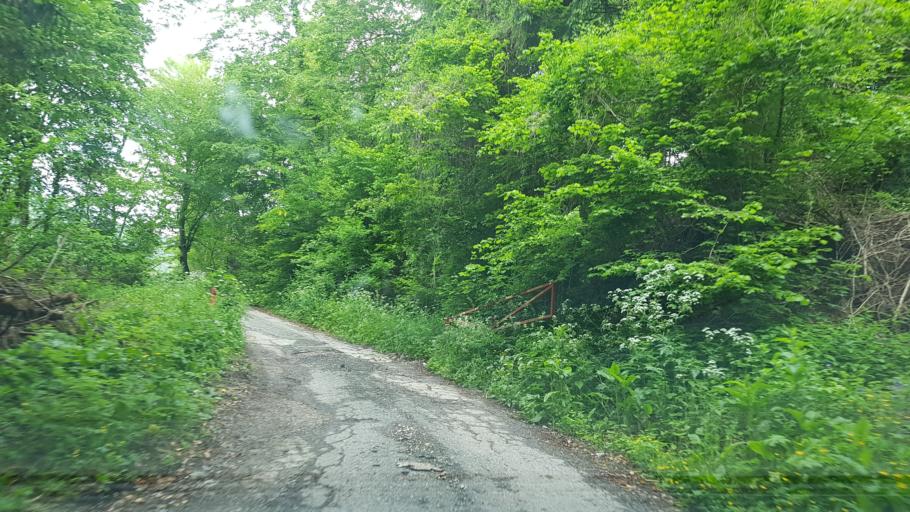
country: IT
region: Friuli Venezia Giulia
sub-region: Provincia di Udine
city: Arta Terme
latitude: 46.4709
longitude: 13.0022
